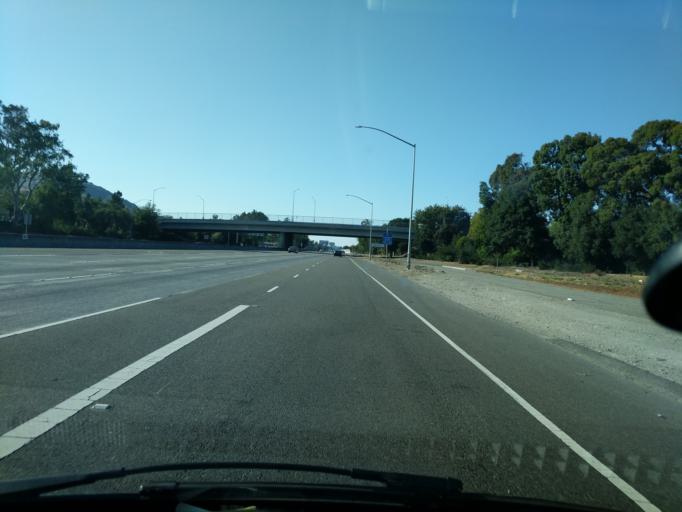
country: US
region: California
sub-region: Contra Costa County
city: San Ramon
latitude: 37.7784
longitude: -121.9757
